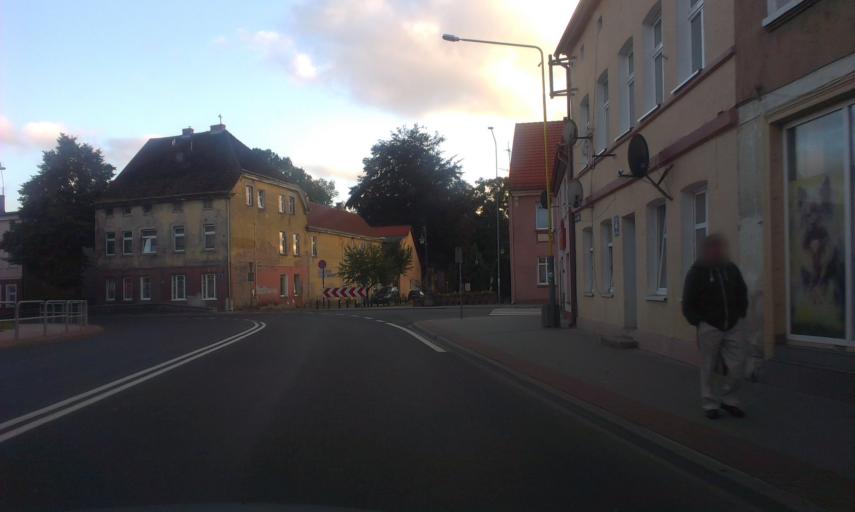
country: PL
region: West Pomeranian Voivodeship
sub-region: Powiat koszalinski
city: Sianow
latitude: 54.2267
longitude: 16.2919
